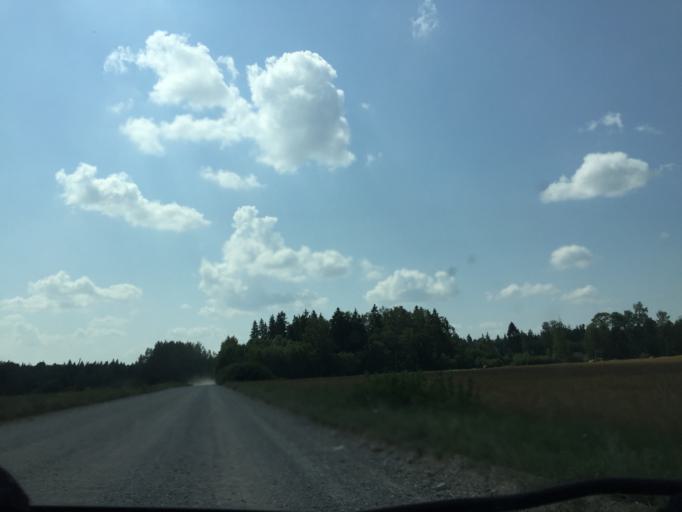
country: LV
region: Tervete
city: Zelmeni
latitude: 56.4001
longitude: 23.3226
